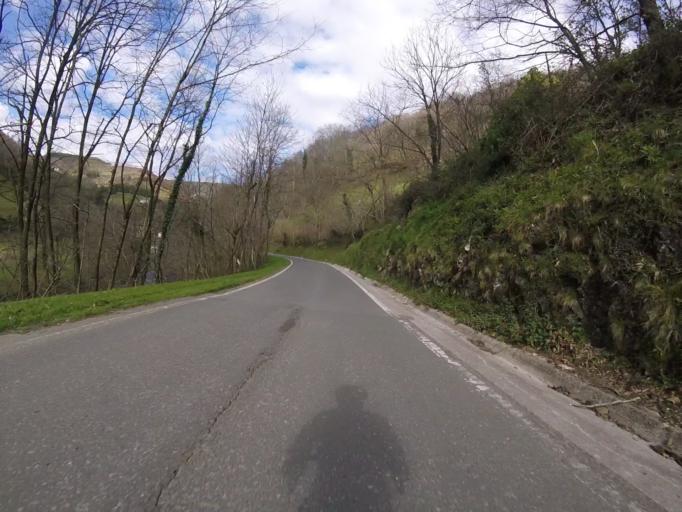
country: ES
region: Navarre
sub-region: Provincia de Navarra
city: Goizueta
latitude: 43.1685
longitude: -1.8589
